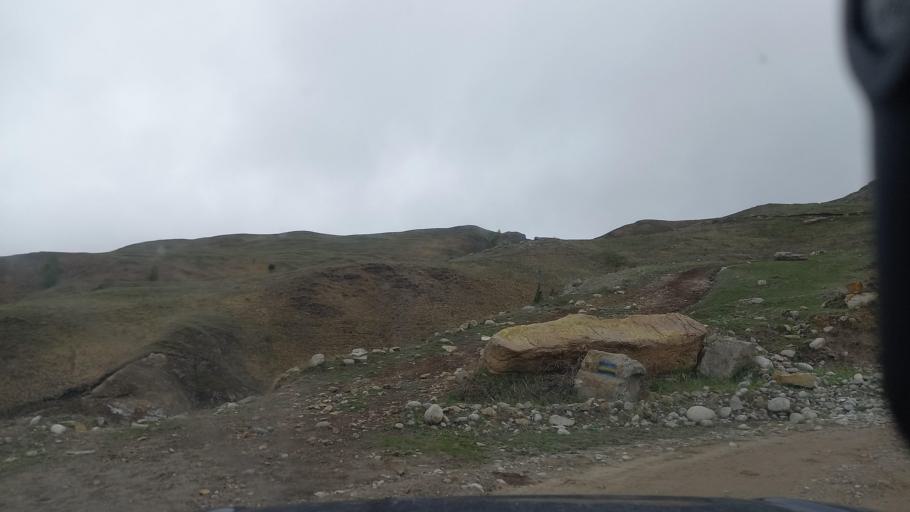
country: RU
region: Kabardino-Balkariya
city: Bylym
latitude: 43.4575
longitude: 42.9949
